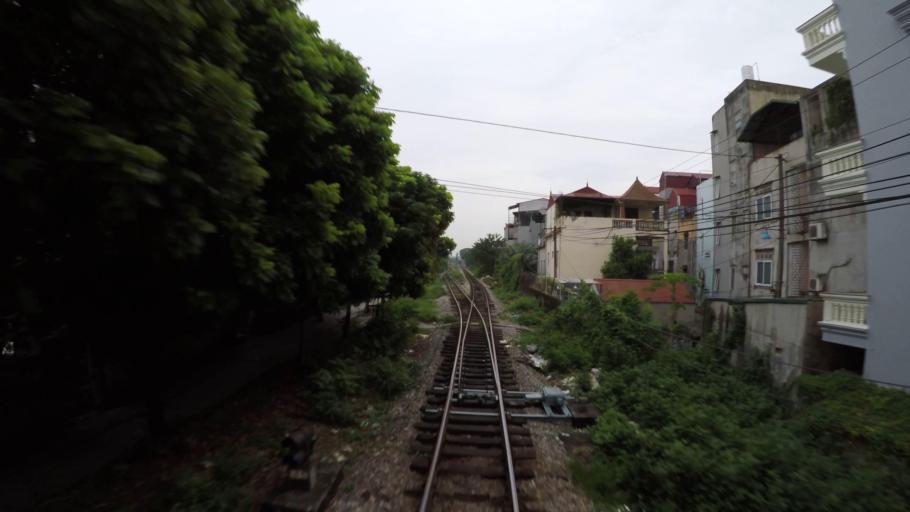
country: VN
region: Ha Noi
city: Trau Quy
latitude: 21.0377
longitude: 105.8986
